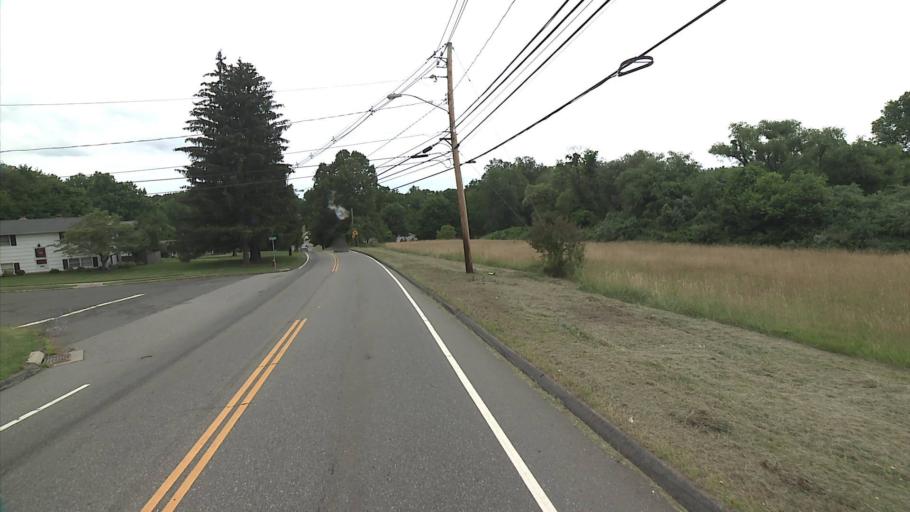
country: US
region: Connecticut
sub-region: New Haven County
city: Wallingford Center
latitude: 41.4351
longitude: -72.8031
